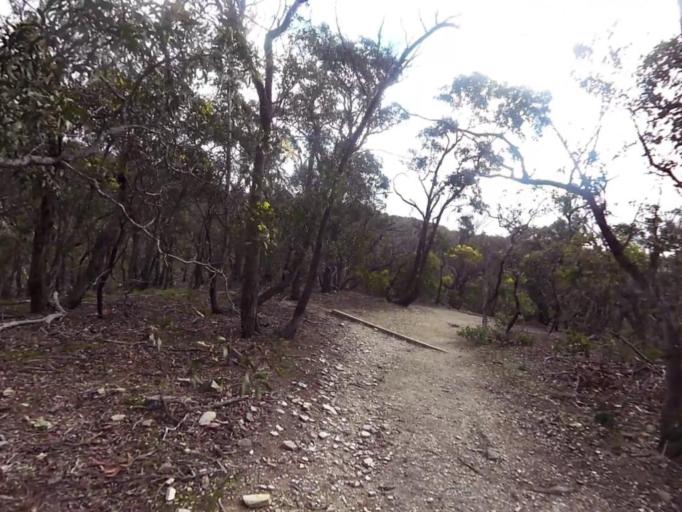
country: AU
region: Victoria
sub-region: Moorabool
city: Bacchus Marsh
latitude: -37.6651
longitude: 144.3342
